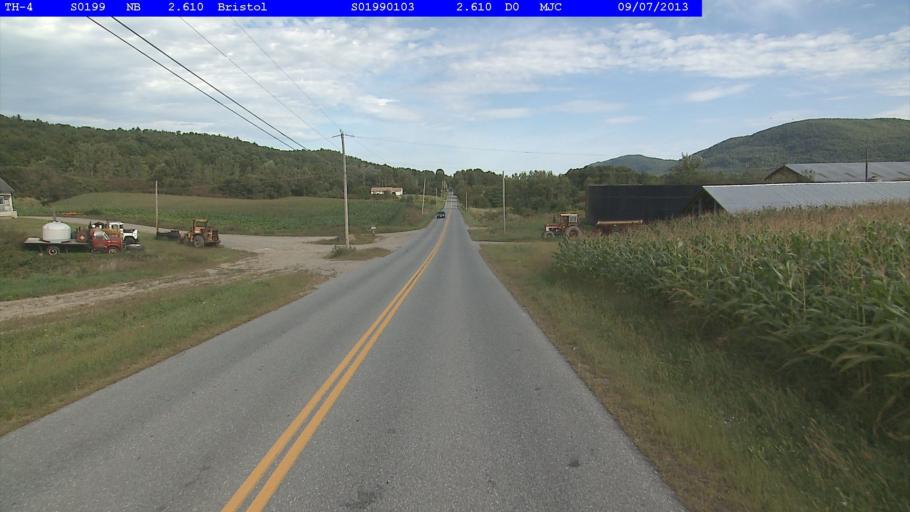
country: US
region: Vermont
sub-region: Addison County
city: Bristol
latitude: 44.1658
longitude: -73.1005
